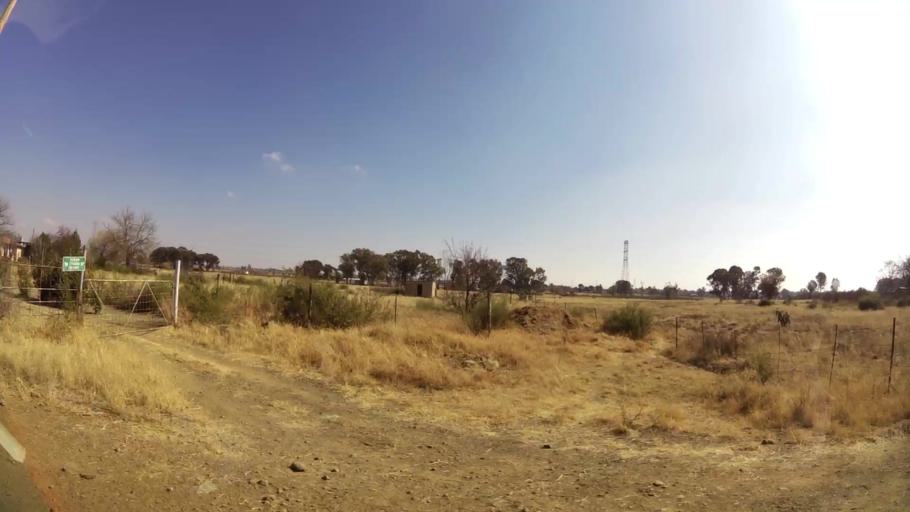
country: ZA
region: Orange Free State
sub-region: Mangaung Metropolitan Municipality
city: Bloemfontein
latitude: -29.1636
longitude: 26.3109
